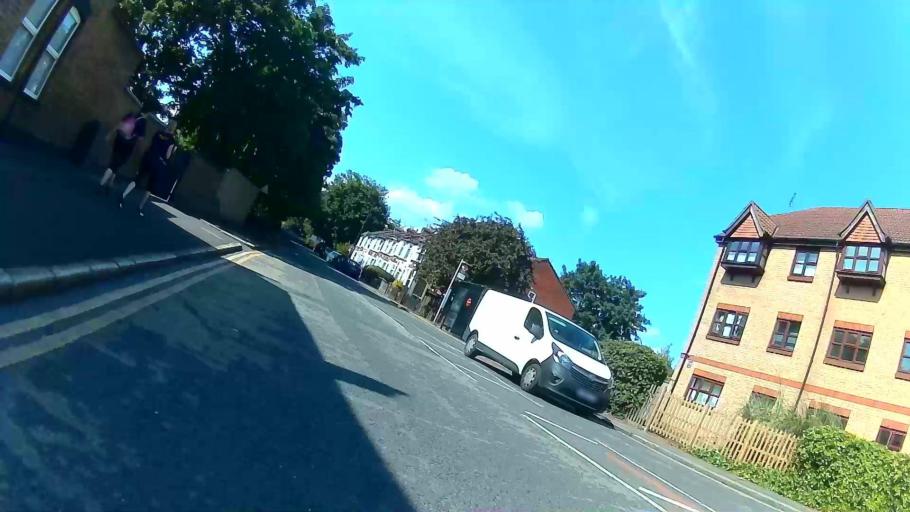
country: GB
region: England
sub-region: Greater London
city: East Ham
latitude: 51.5256
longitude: 0.0180
